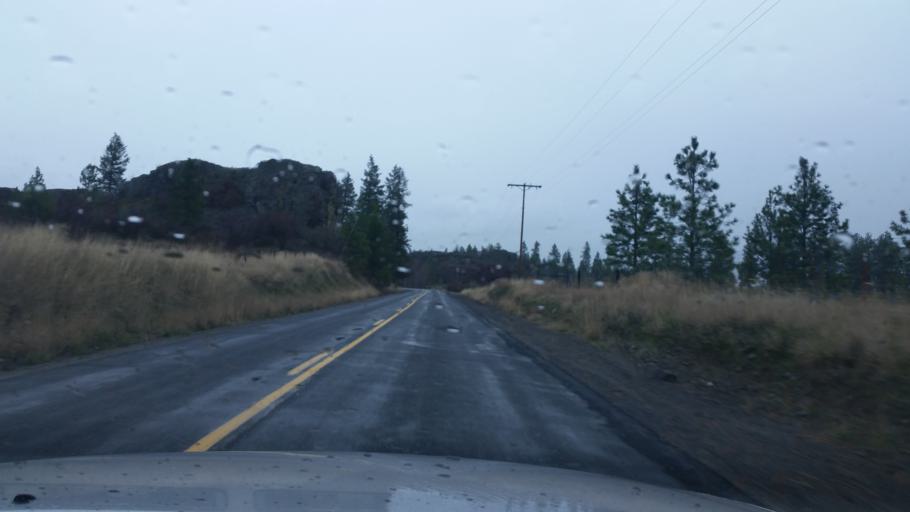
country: US
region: Washington
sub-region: Spokane County
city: Airway Heights
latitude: 47.6949
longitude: -117.5719
